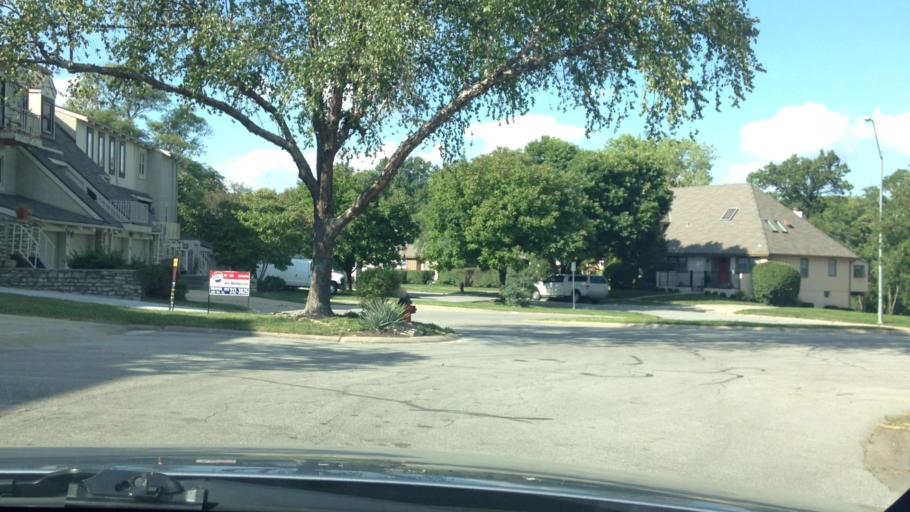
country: US
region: Missouri
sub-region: Jackson County
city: Grandview
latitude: 38.8908
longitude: -94.5901
